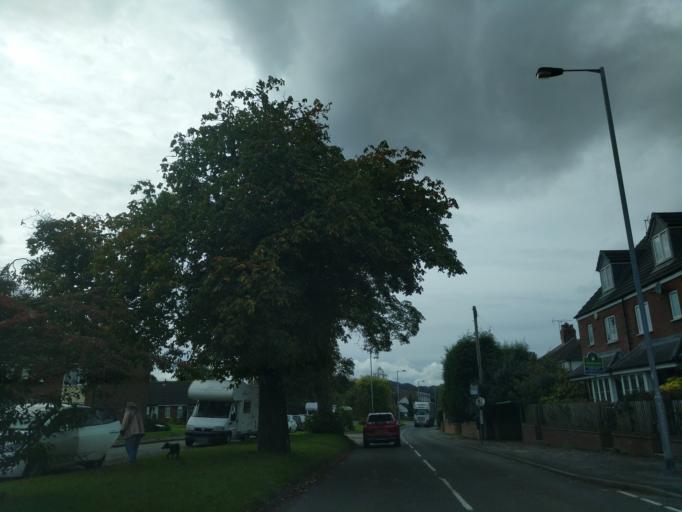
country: GB
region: England
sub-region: Staffordshire
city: Audley
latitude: 53.0029
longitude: -2.3371
